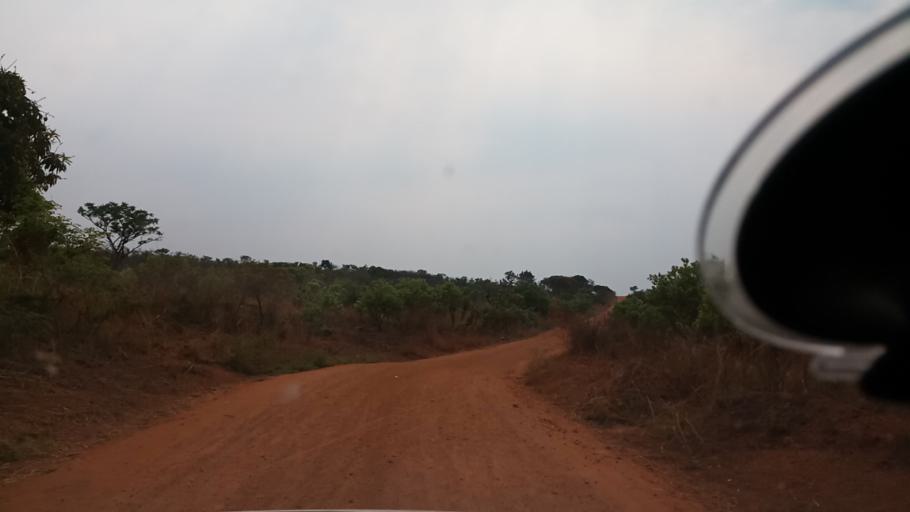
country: ZM
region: Luapula
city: Nchelenge
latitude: -9.0982
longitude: 28.3109
